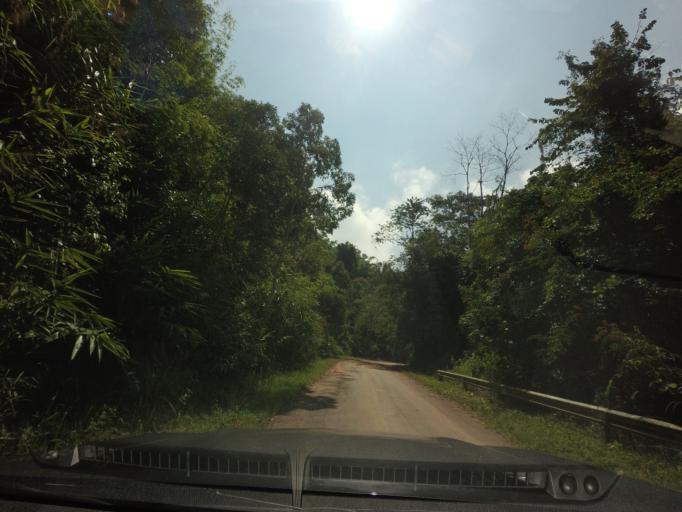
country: TH
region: Loei
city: Na Haeo
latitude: 17.5196
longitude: 100.9385
